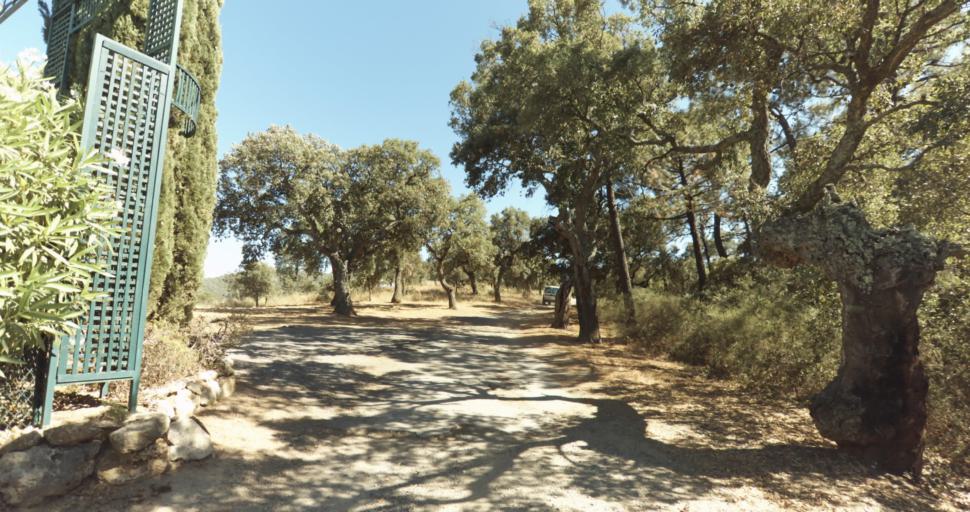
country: FR
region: Provence-Alpes-Cote d'Azur
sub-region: Departement du Var
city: Gassin
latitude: 43.2350
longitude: 6.5852
